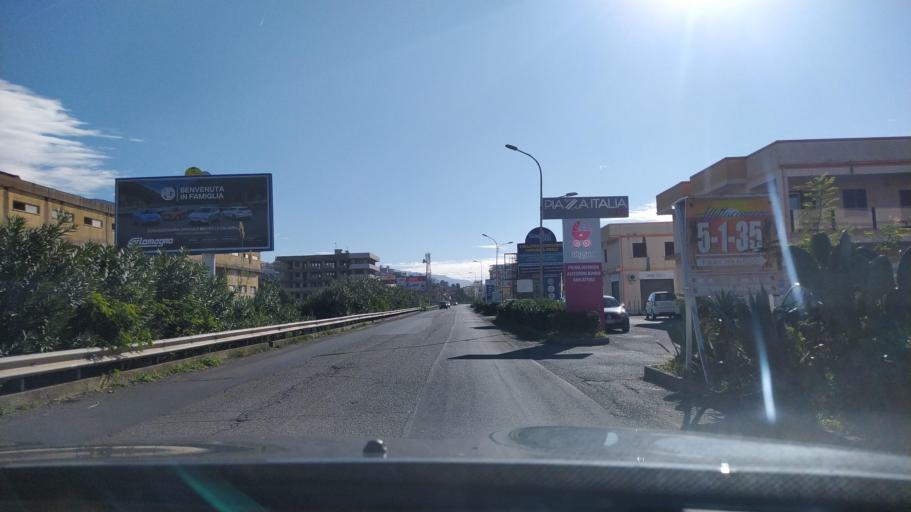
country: IT
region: Calabria
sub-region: Provincia di Cosenza
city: Paola
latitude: 39.3738
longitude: 16.0269
